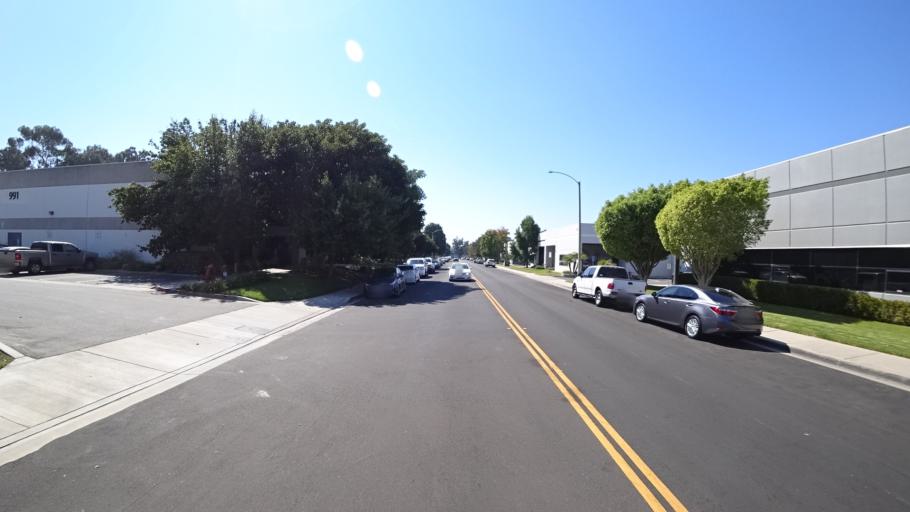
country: US
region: California
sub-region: Orange County
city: San Clemente
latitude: 33.4539
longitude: -117.6023
